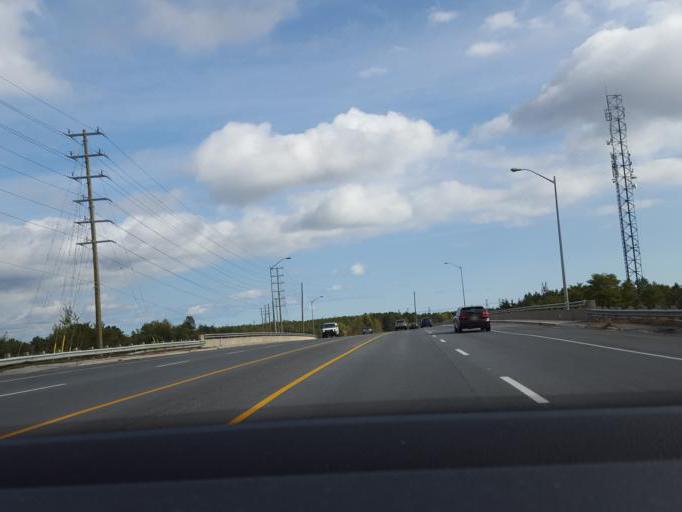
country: CA
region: Ontario
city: Pickering
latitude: 43.8878
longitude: -79.0818
